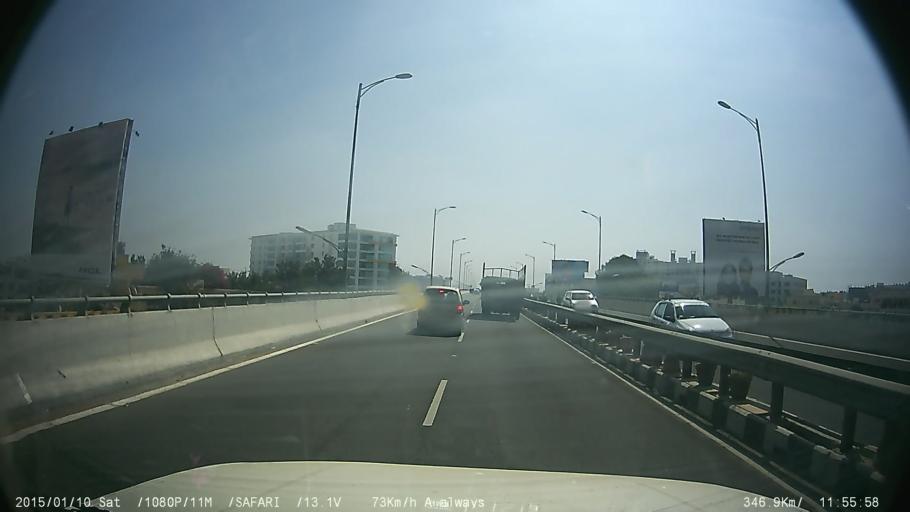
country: IN
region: Karnataka
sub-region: Bangalore Urban
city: Bangalore
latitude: 12.8682
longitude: 77.6548
